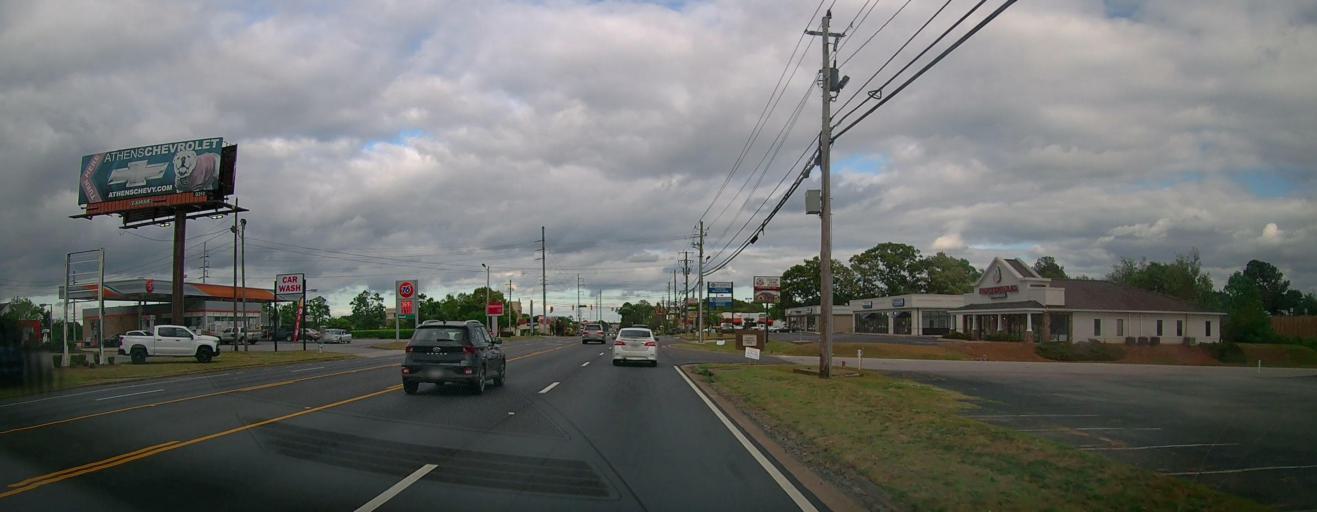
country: US
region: Georgia
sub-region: Oconee County
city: Bogart
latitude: 33.9404
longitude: -83.4773
